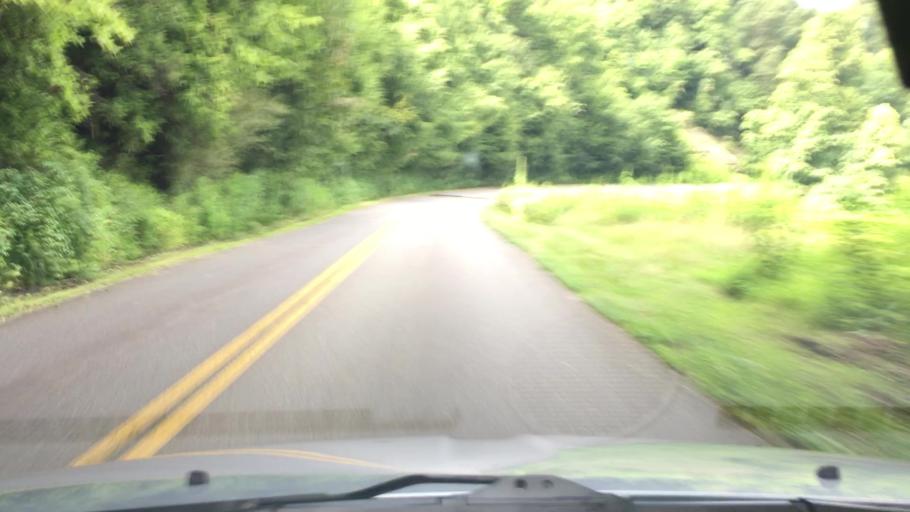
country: US
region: North Carolina
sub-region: Buncombe County
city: Black Mountain
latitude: 35.7405
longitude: -82.1894
